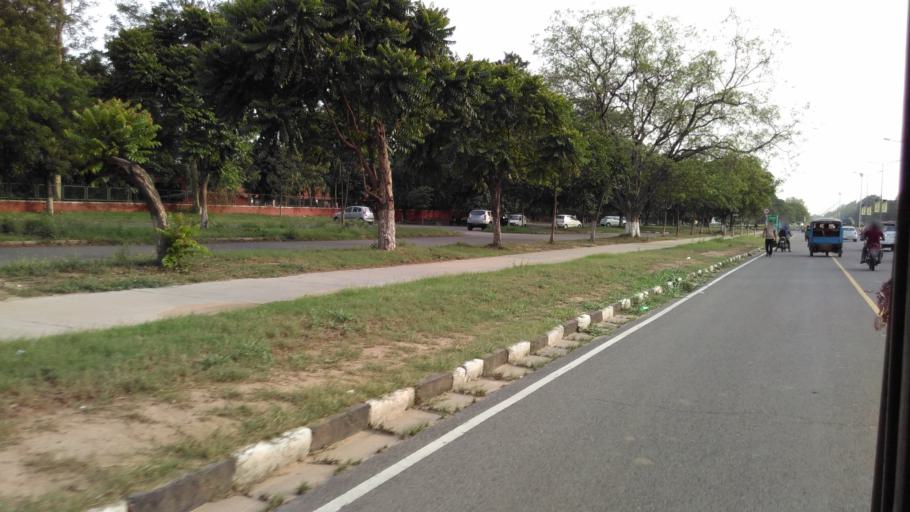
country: IN
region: Chandigarh
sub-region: Chandigarh
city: Chandigarh
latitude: 30.7479
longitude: 76.7878
